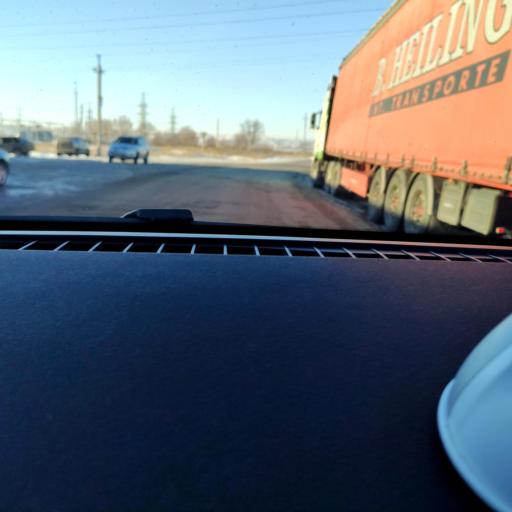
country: RU
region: Samara
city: Spiridonovka
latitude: 53.1062
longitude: 50.6427
